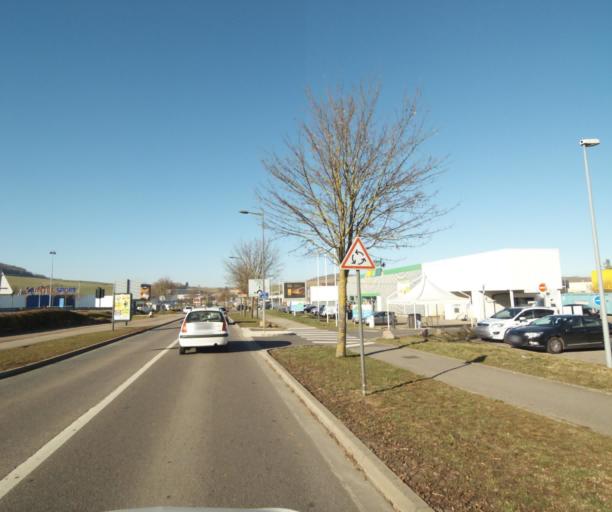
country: FR
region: Lorraine
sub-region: Departement de Meurthe-et-Moselle
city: Pulnoy
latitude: 48.7053
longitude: 6.2456
